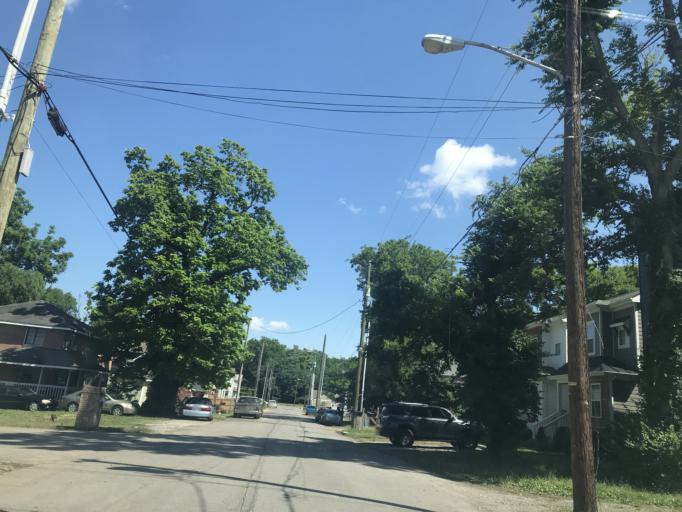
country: US
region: Tennessee
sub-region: Davidson County
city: Nashville
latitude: 36.1818
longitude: -86.8084
